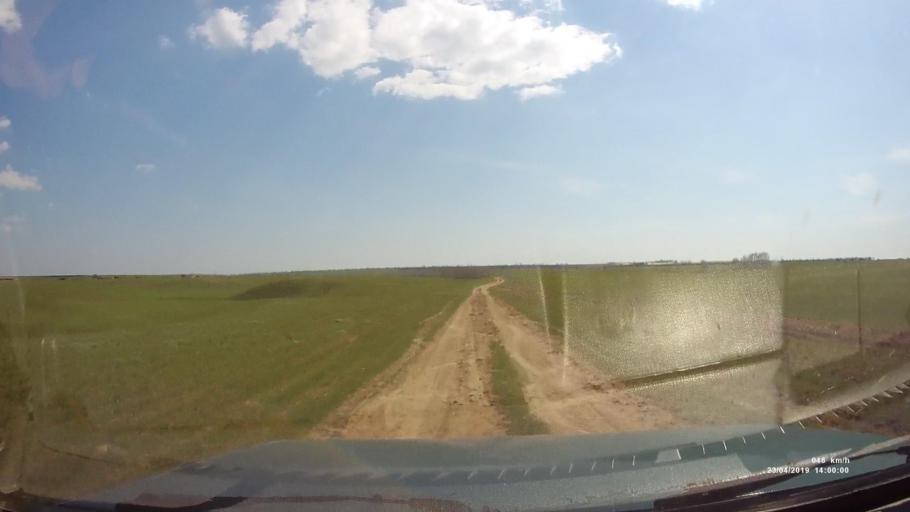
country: RU
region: Rostov
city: Remontnoye
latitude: 46.5626
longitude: 42.9468
